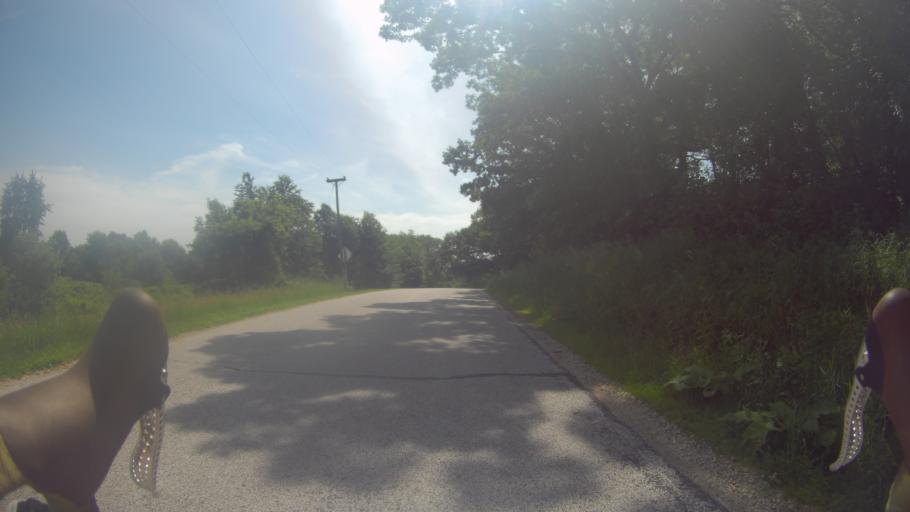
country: US
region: Wisconsin
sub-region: Jefferson County
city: Cambridge
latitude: 43.0550
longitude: -89.0195
